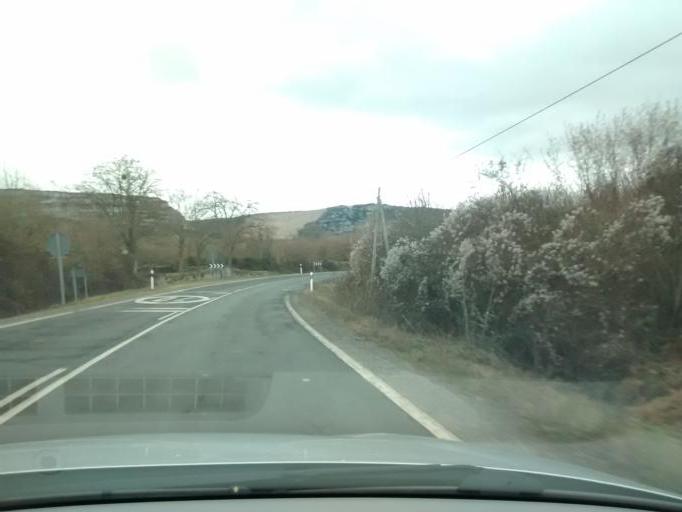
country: ES
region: Castille and Leon
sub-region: Provincia de Burgos
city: Espinosa de los Monteros
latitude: 43.0596
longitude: -3.4928
